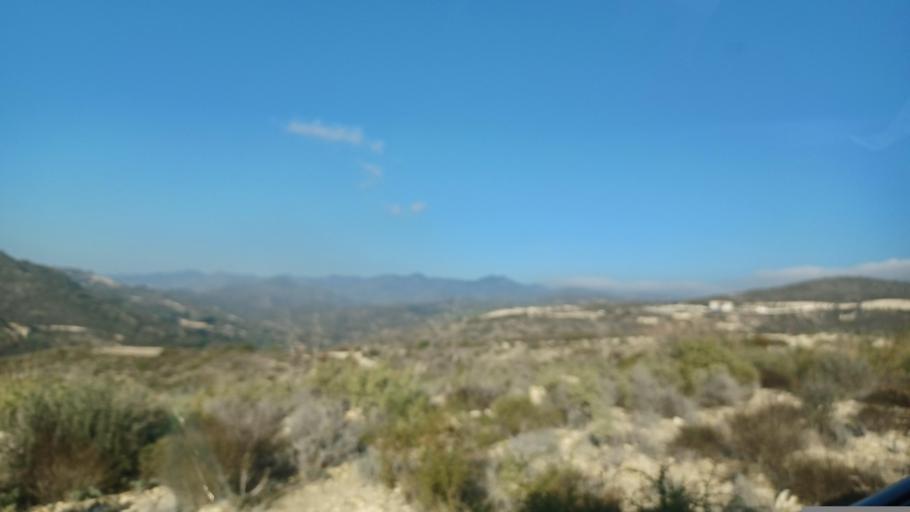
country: CY
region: Larnaka
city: Kofinou
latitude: 34.8359
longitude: 33.3025
